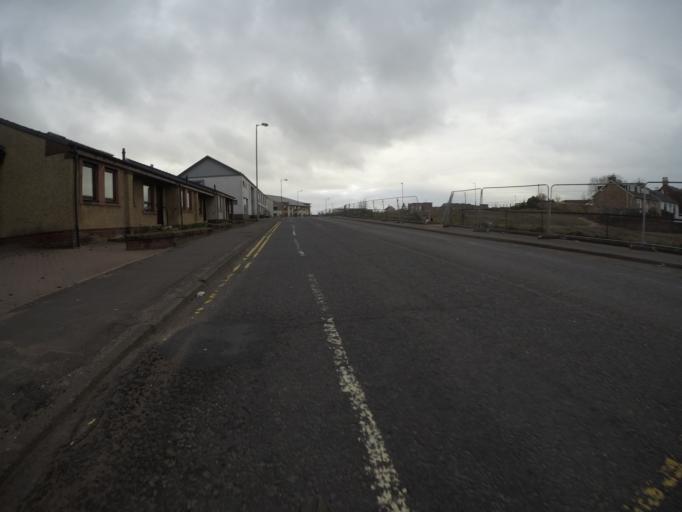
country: GB
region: Scotland
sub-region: East Ayrshire
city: Kilmarnock
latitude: 55.6155
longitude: -4.4968
